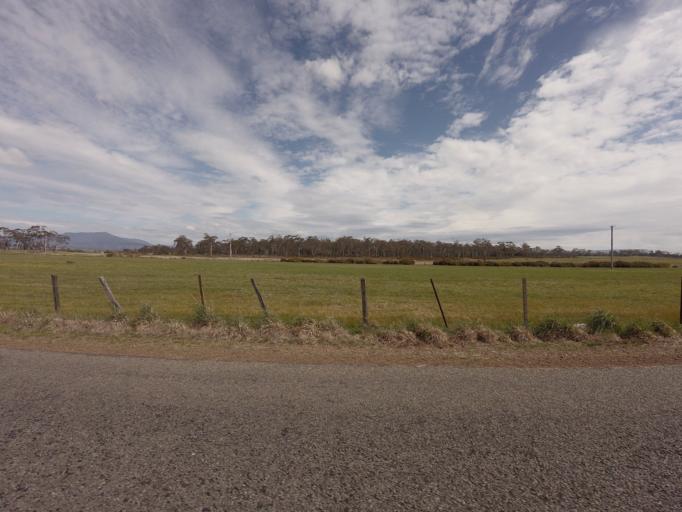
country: AU
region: Tasmania
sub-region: Northern Midlands
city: Longford
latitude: -41.7346
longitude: 147.1980
